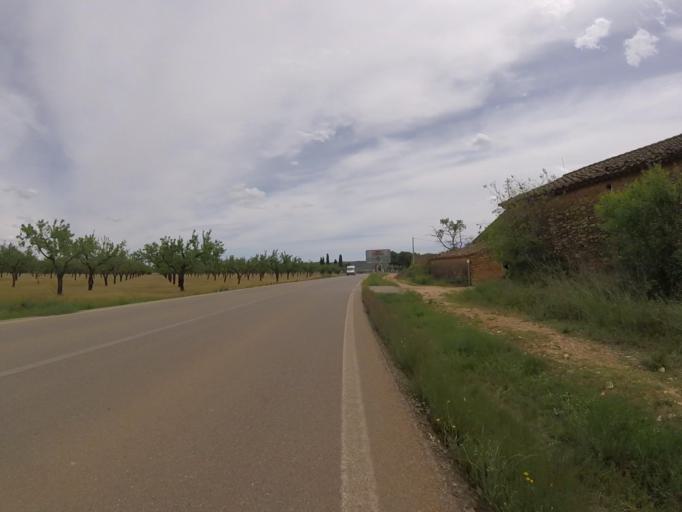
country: ES
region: Valencia
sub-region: Provincia de Castello
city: Cabanes
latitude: 40.1658
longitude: 0.0129
